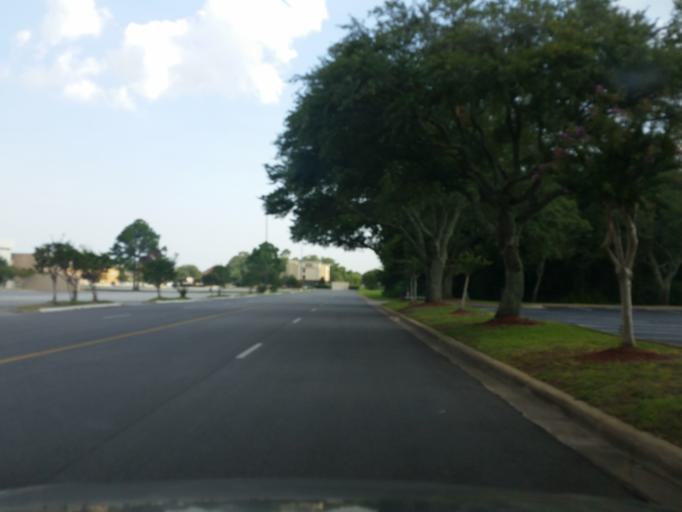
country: US
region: Florida
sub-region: Escambia County
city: Ferry Pass
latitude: 30.5002
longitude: -87.2264
